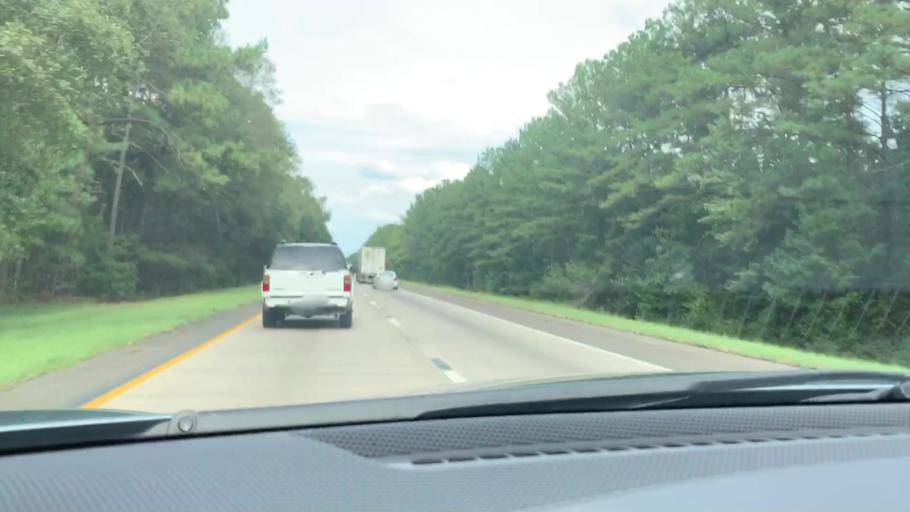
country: US
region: South Carolina
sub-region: Hampton County
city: Yemassee
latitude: 32.7641
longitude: -80.8121
